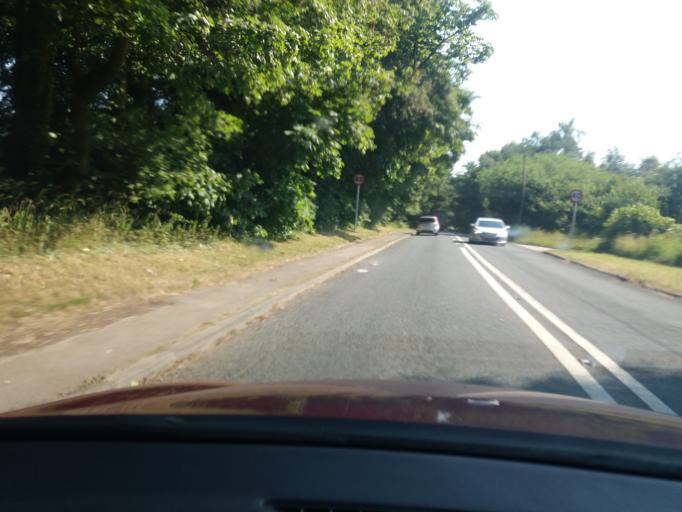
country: GB
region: England
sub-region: Lancashire
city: Clayton-le-Woods
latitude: 53.6869
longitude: -2.6558
